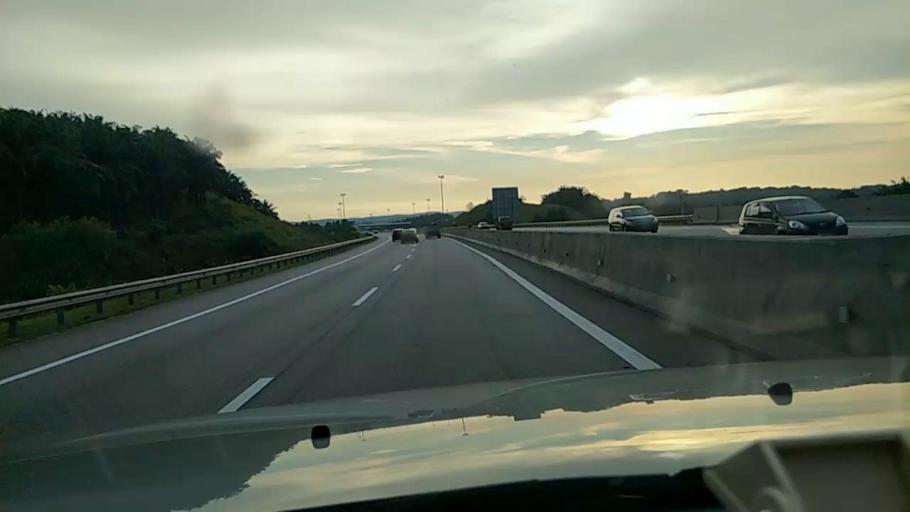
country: MY
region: Selangor
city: Kuang
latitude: 3.2717
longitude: 101.5376
